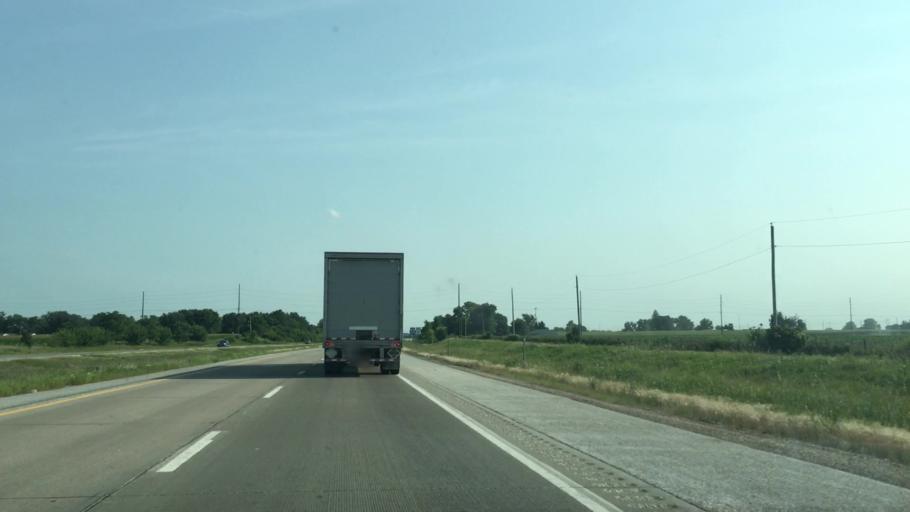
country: US
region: Iowa
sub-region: Scott County
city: Walcott
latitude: 41.5853
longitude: -90.6762
